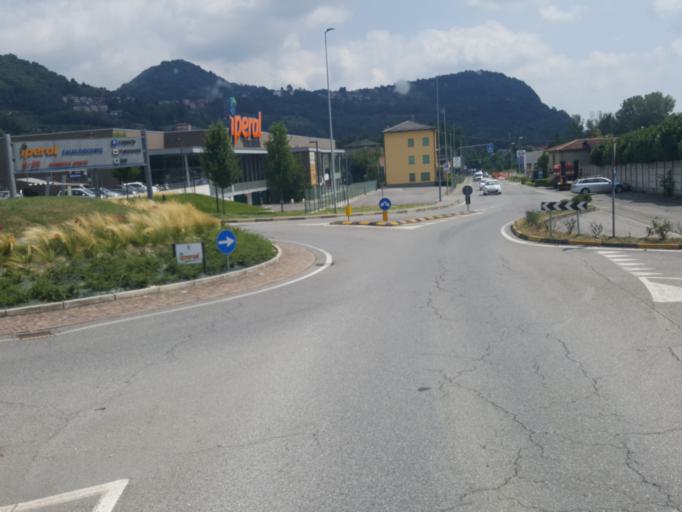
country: IT
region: Lombardy
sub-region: Provincia di Lecco
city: Calolziocorte
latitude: 45.7906
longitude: 9.4393
